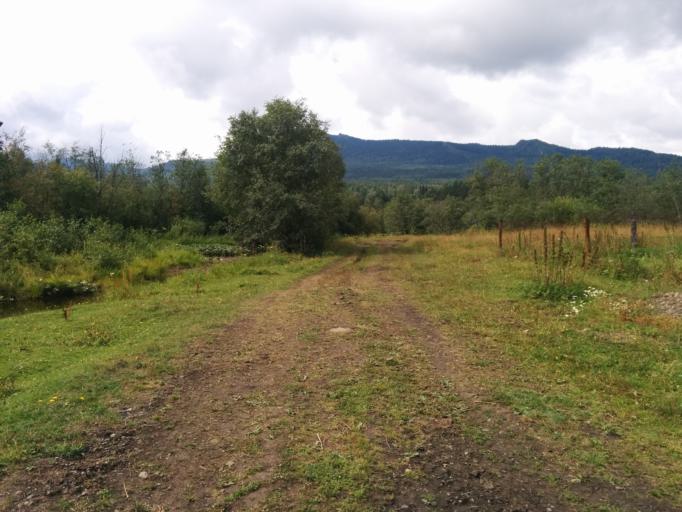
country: RU
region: Bashkortostan
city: Beloretsk
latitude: 54.0462
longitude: 58.3284
